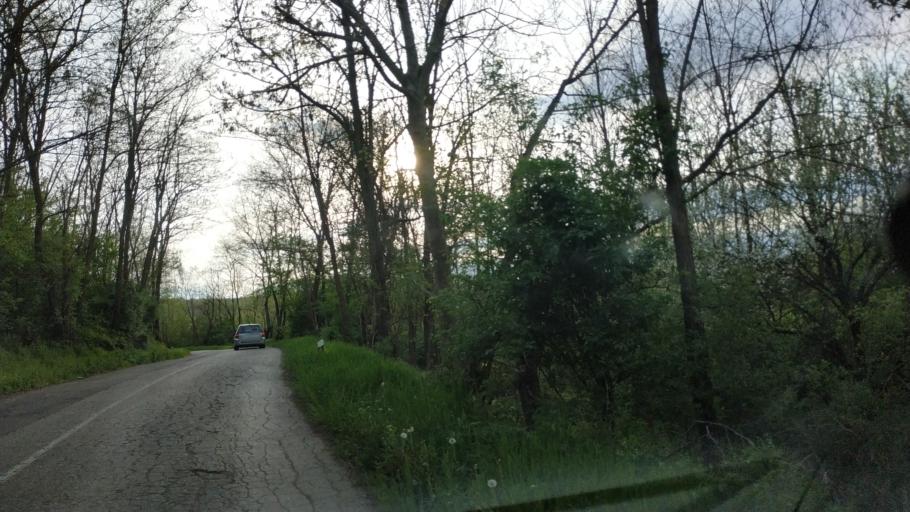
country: RS
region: Central Serbia
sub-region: Nisavski Okrug
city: Aleksinac
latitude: 43.4808
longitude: 21.8133
